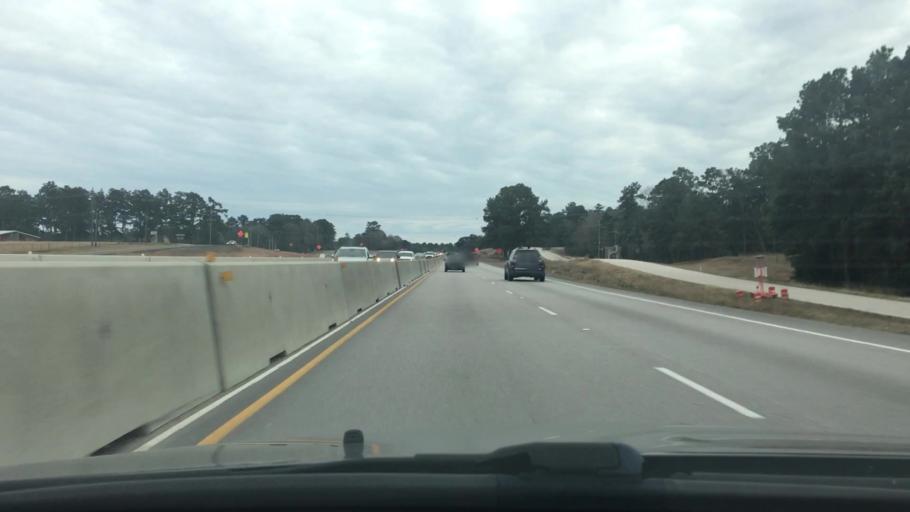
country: US
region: Texas
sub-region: Walker County
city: Huntsville
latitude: 30.6701
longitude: -95.5165
